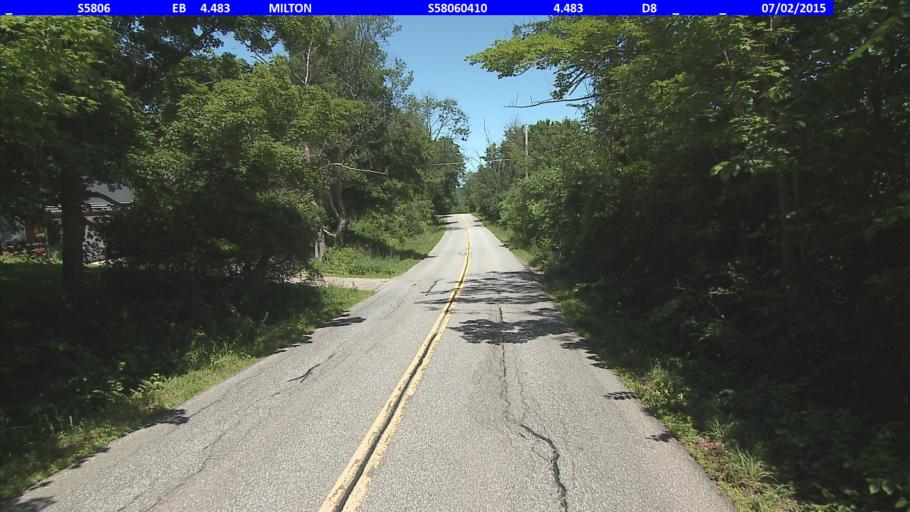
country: US
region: Vermont
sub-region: Chittenden County
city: Milton
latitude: 44.6854
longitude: -73.1764
